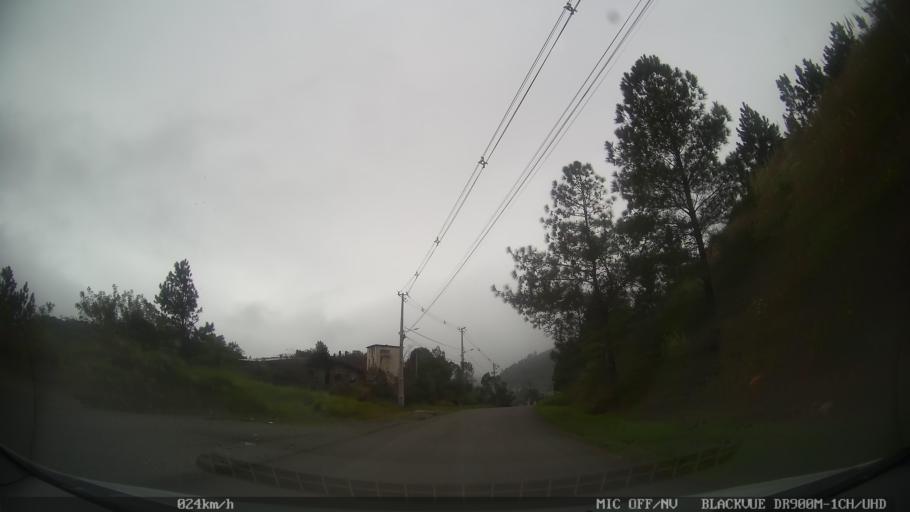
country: BR
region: Parana
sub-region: Campina Grande Do Sul
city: Campina Grande do Sul
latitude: -25.1083
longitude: -48.8327
